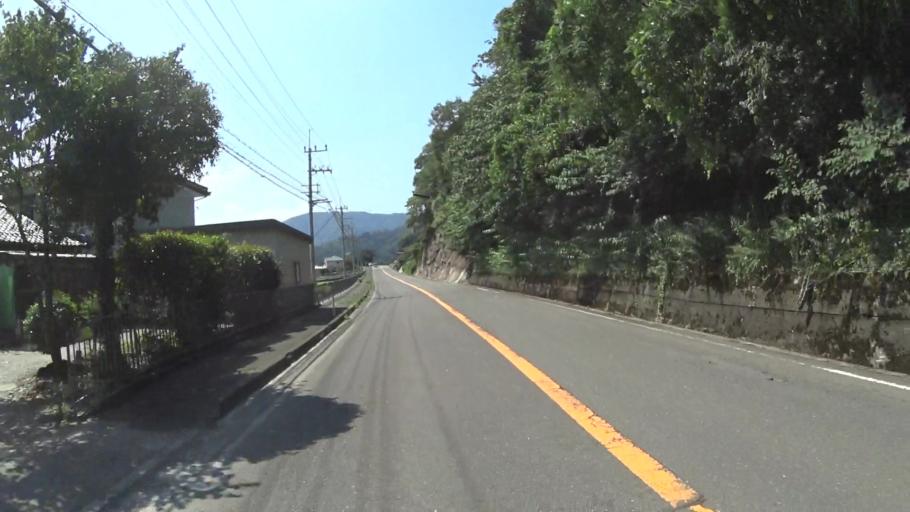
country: JP
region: Fukui
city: Obama
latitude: 35.4054
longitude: 135.6607
